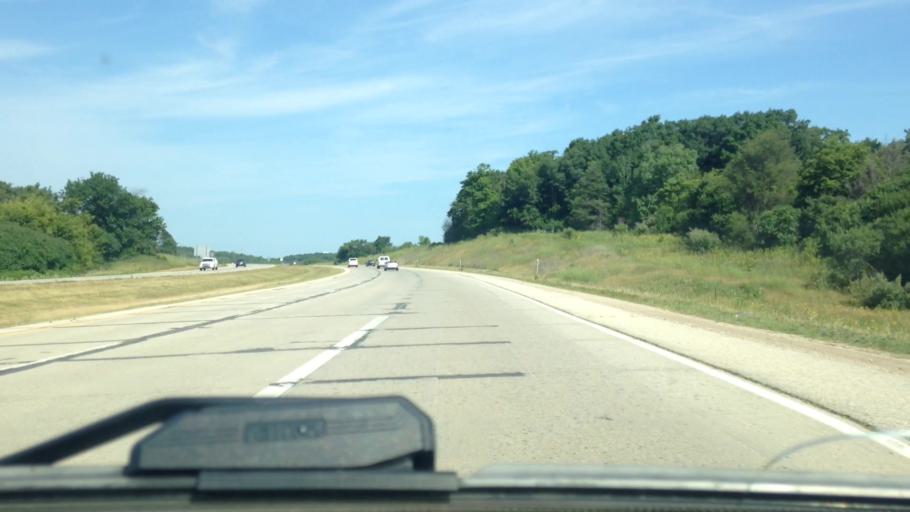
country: US
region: Wisconsin
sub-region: Washington County
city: West Bend
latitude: 43.4035
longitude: -88.1939
